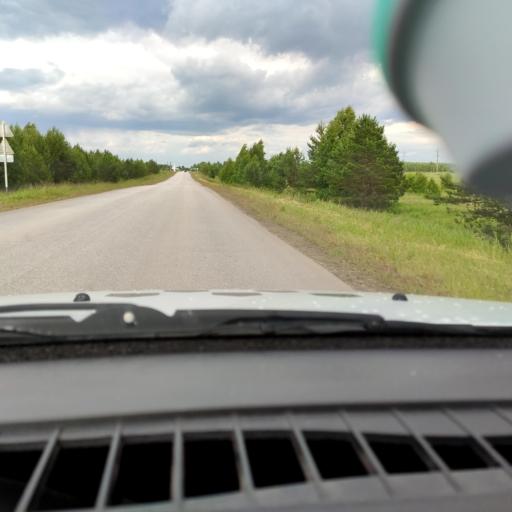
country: RU
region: Perm
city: Orda
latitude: 57.1371
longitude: 56.7178
